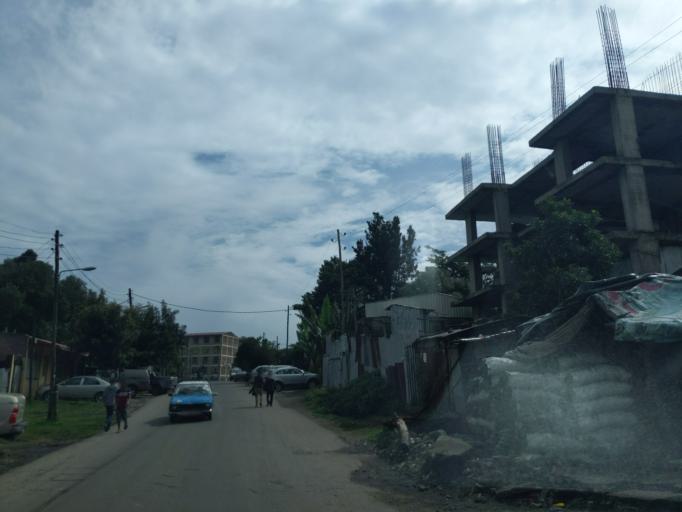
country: ET
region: Adis Abeba
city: Addis Ababa
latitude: 9.0014
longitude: 38.7566
